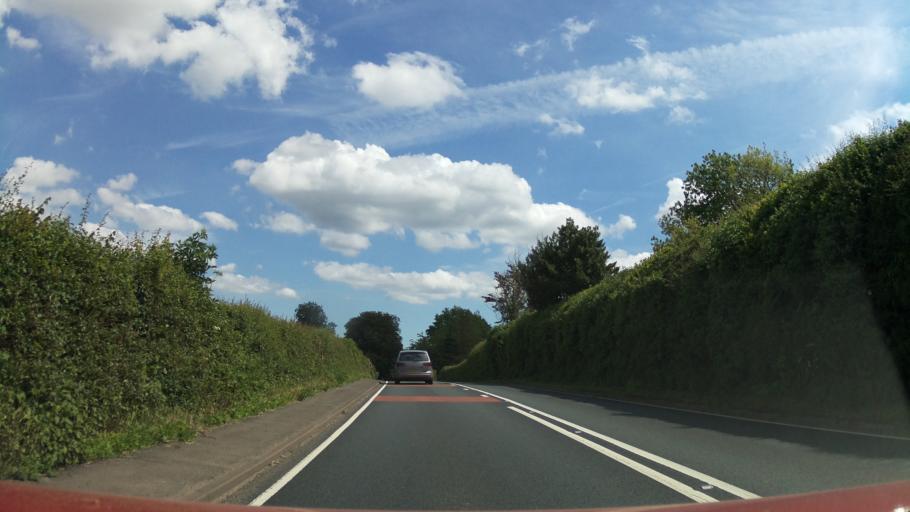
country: GB
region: England
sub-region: Herefordshire
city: Sellack
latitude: 51.9202
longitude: -2.6396
